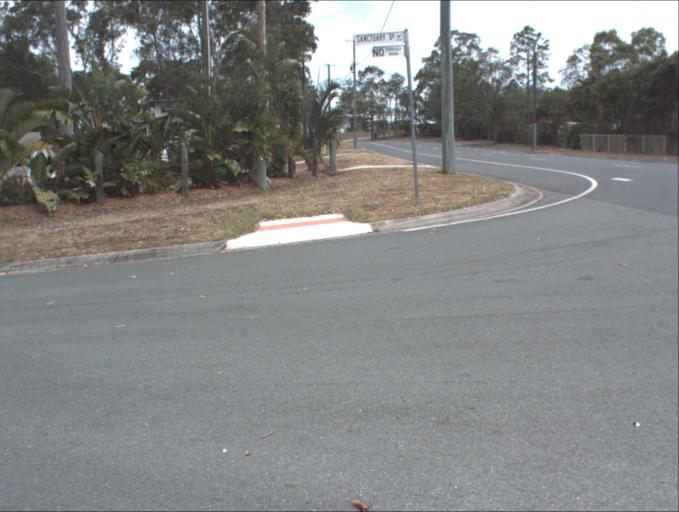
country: AU
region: Queensland
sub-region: Logan
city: Beenleigh
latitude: -27.6710
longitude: 153.2234
